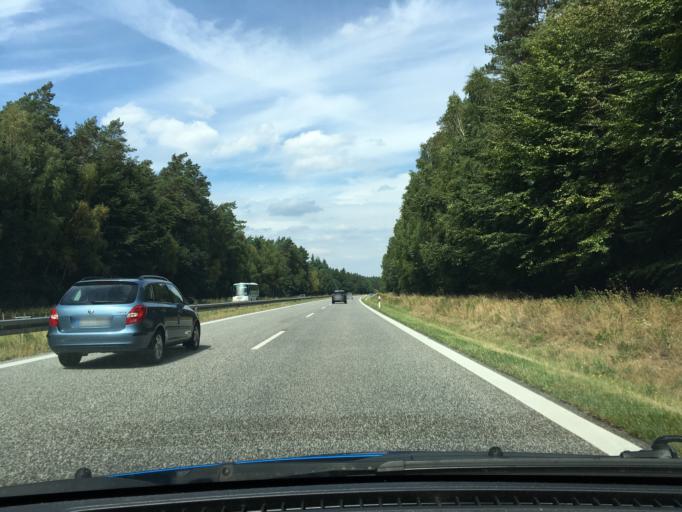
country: DE
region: Mecklenburg-Vorpommern
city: Mirow
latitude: 53.5136
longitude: 11.4697
